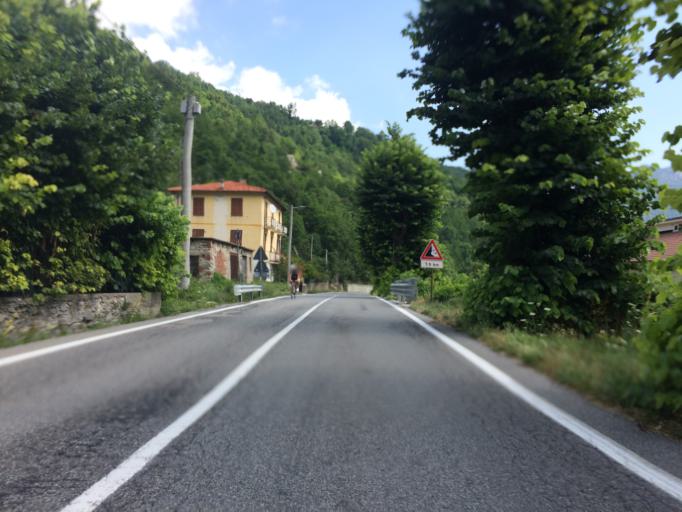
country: IT
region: Piedmont
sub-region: Provincia di Cuneo
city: Ormea
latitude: 44.1591
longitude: 7.9572
